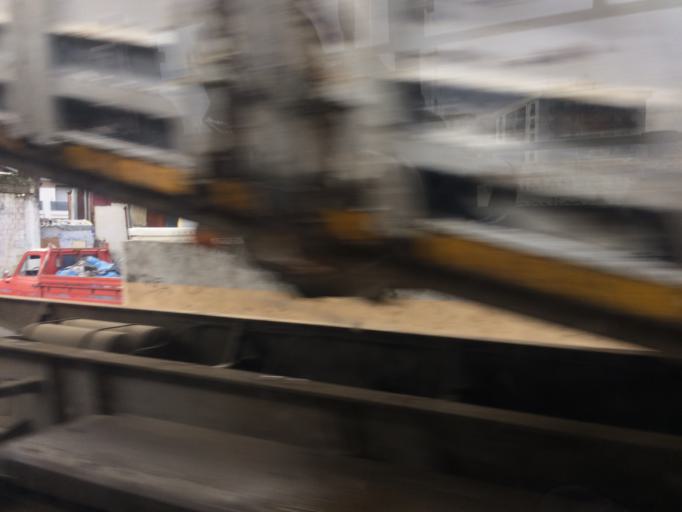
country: TR
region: Izmir
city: Karsiyaka
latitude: 38.5173
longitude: 27.0413
